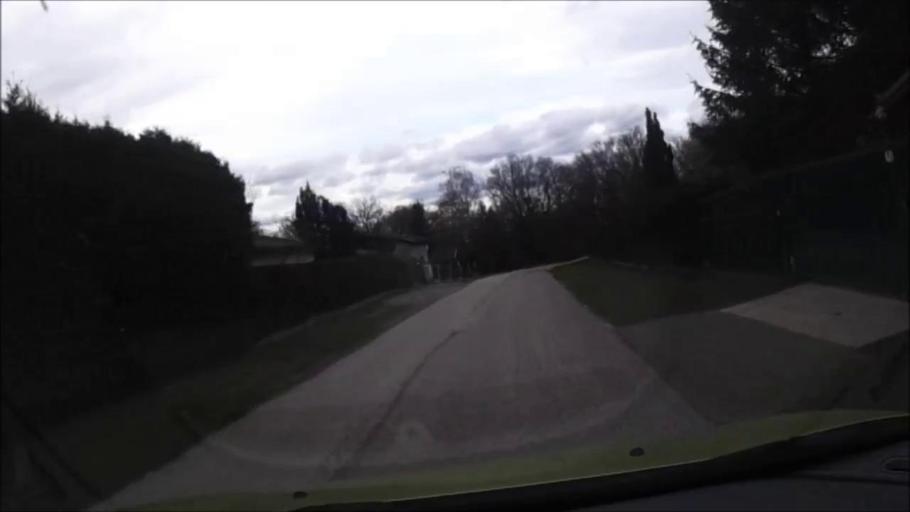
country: AT
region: Burgenland
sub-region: Eisenstadt-Umgebung
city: Loretto
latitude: 47.9006
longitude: 16.5183
